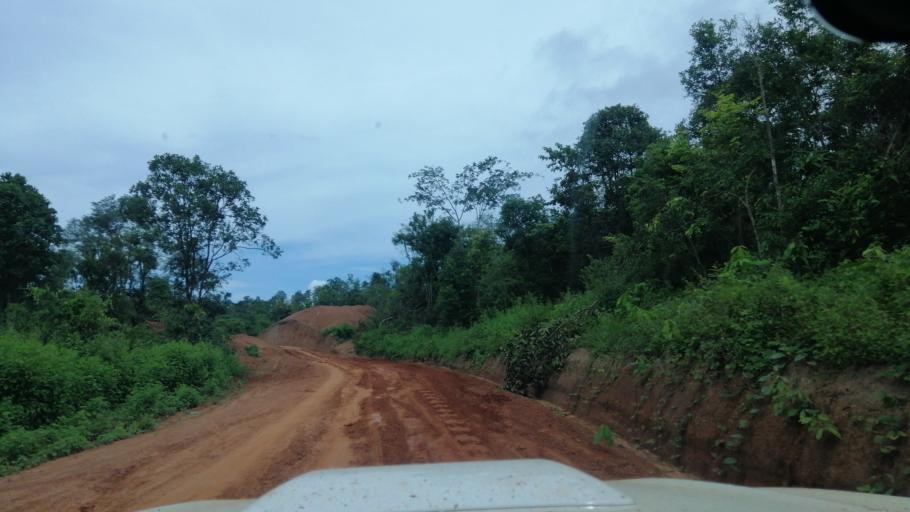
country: TH
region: Loei
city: Na Haeo
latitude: 17.5801
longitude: 101.1518
